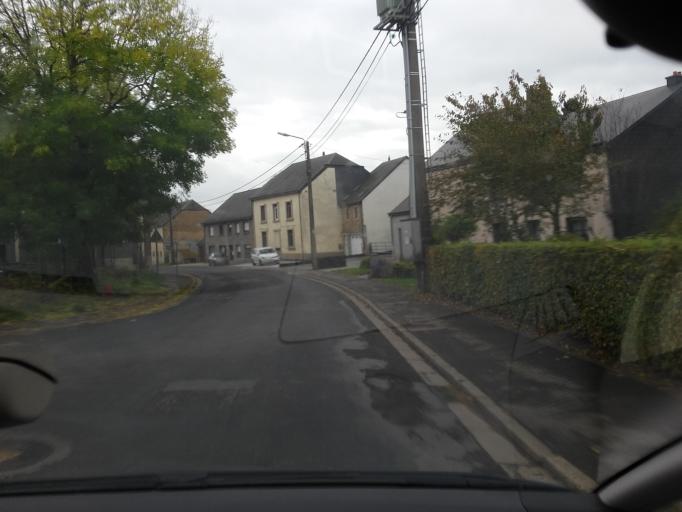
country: BE
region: Wallonia
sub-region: Province du Luxembourg
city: Attert
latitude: 49.7012
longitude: 5.7455
